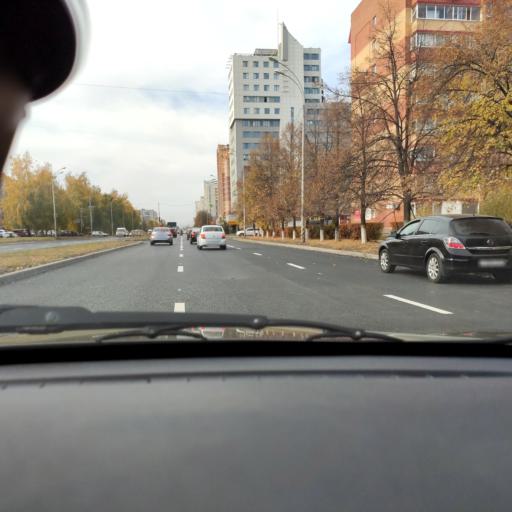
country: RU
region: Samara
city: Tol'yatti
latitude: 53.5131
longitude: 49.2998
